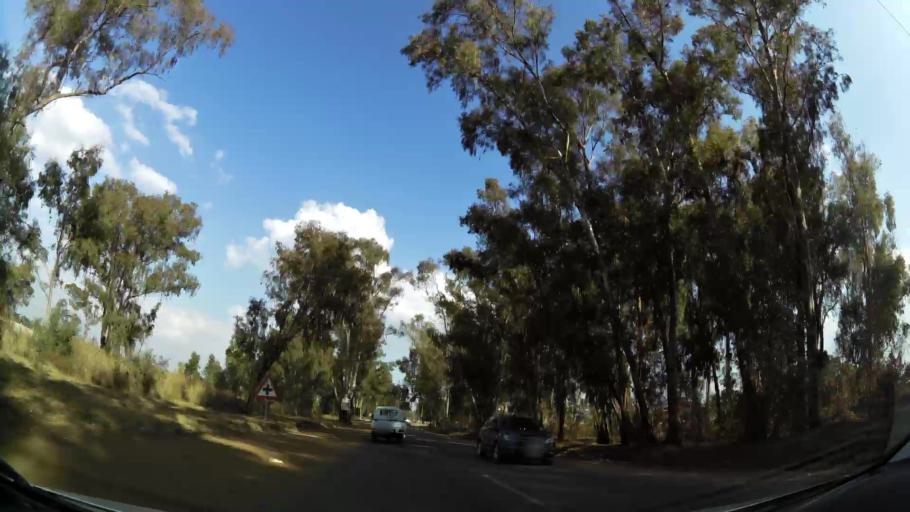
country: ZA
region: Gauteng
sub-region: Ekurhuleni Metropolitan Municipality
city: Tembisa
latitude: -25.9398
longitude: 28.2330
